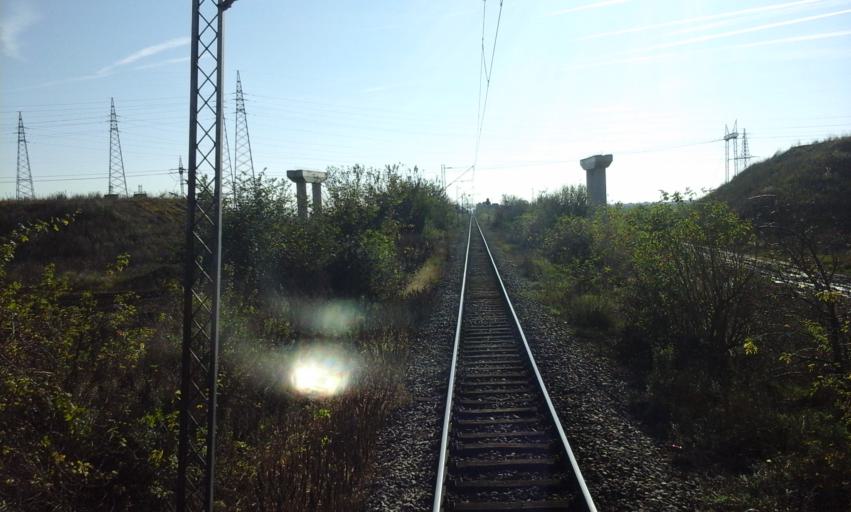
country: RS
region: Autonomna Pokrajina Vojvodina
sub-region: Severnobacki Okrug
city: Subotica
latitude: 46.0346
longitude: 19.6829
